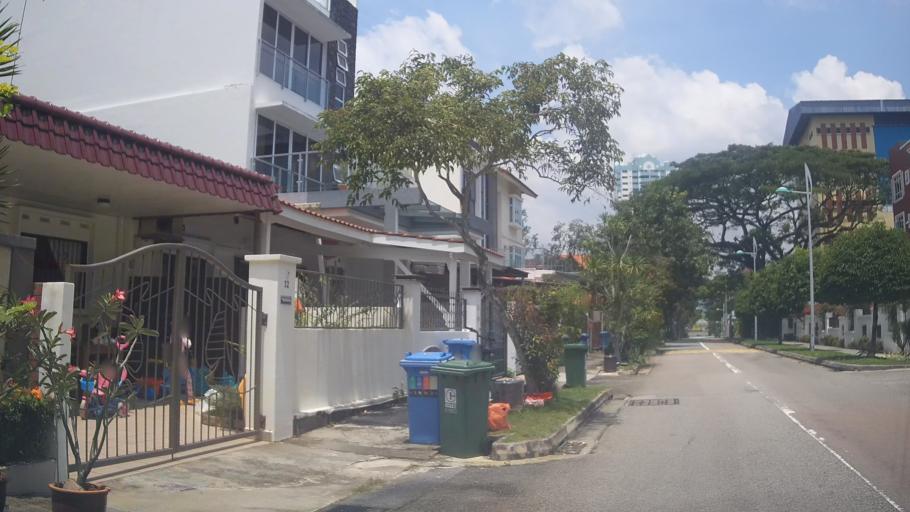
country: SG
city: Singapore
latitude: 1.3419
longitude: 103.7732
